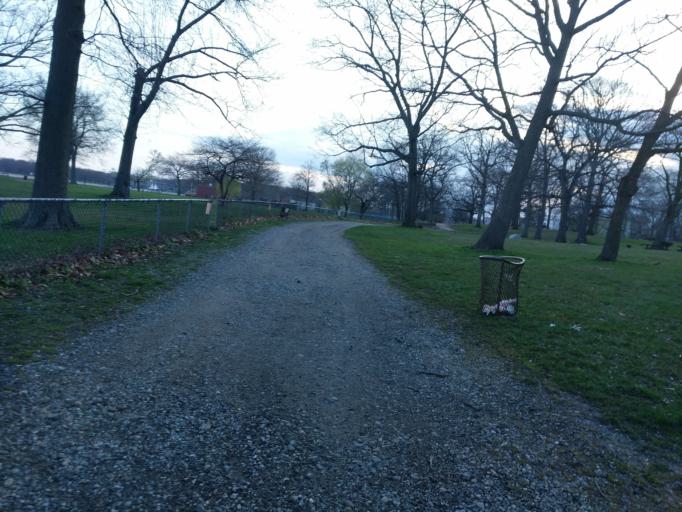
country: US
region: New York
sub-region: Westchester County
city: Pelham Manor
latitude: 40.8709
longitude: -73.7889
